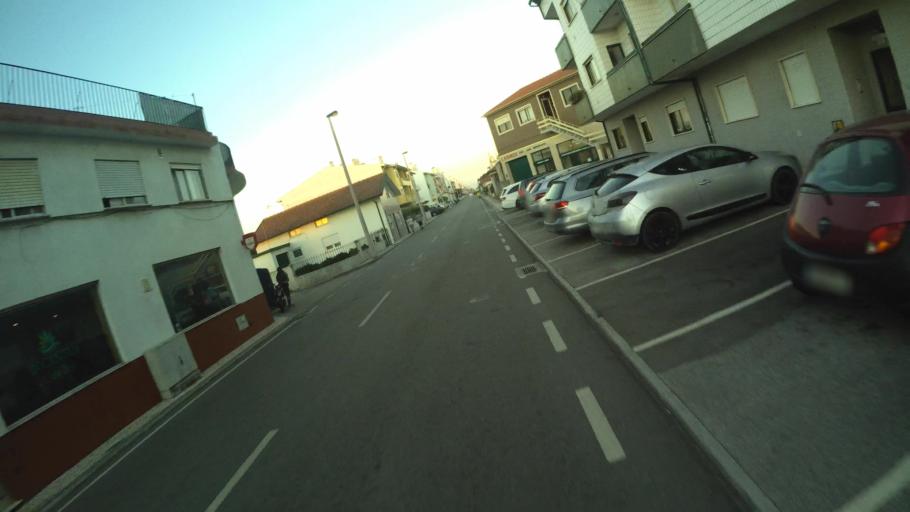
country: PT
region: Aveiro
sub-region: Ilhavo
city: Gafanha da Nazare
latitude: 40.6378
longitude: -8.7198
